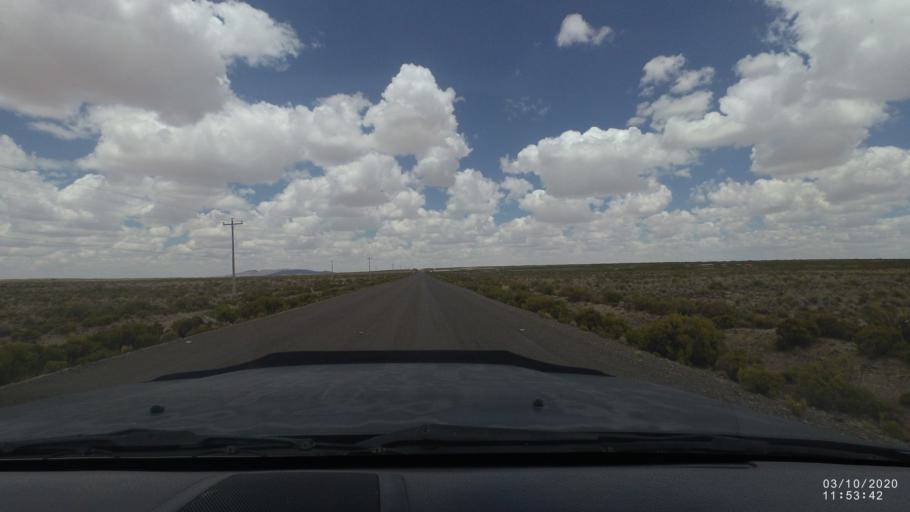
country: BO
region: Oruro
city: Poopo
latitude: -18.4833
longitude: -67.6054
